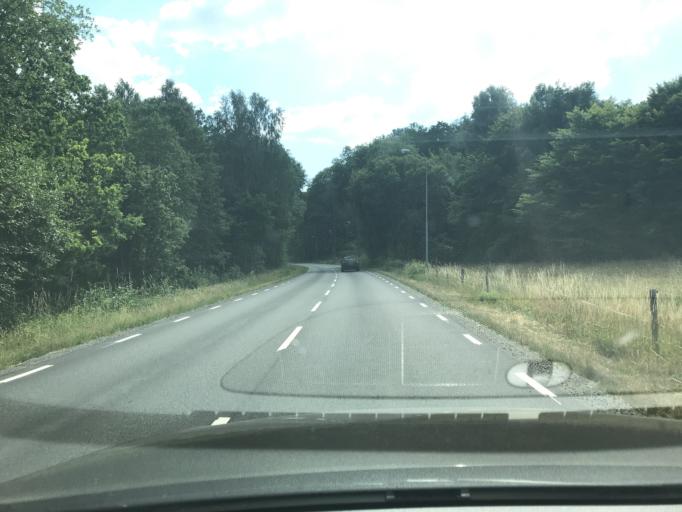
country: SE
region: Skane
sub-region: Hassleholms Kommun
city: Hastveda
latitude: 56.2875
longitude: 13.9176
